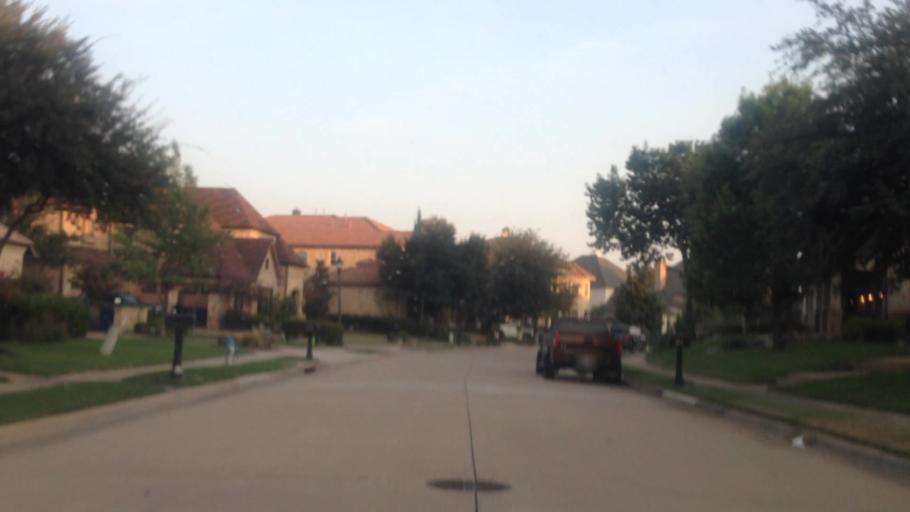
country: US
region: Texas
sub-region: Denton County
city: The Colony
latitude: 33.1238
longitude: -96.8788
